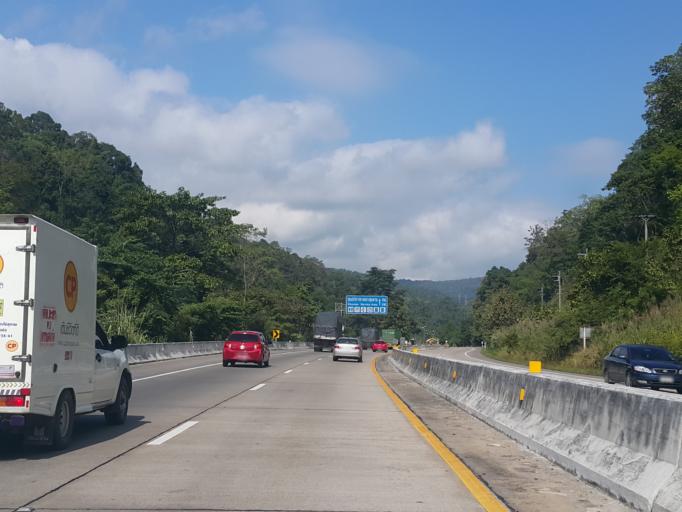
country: TH
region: Lamphun
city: Mae Tha
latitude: 18.3833
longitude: 99.2214
